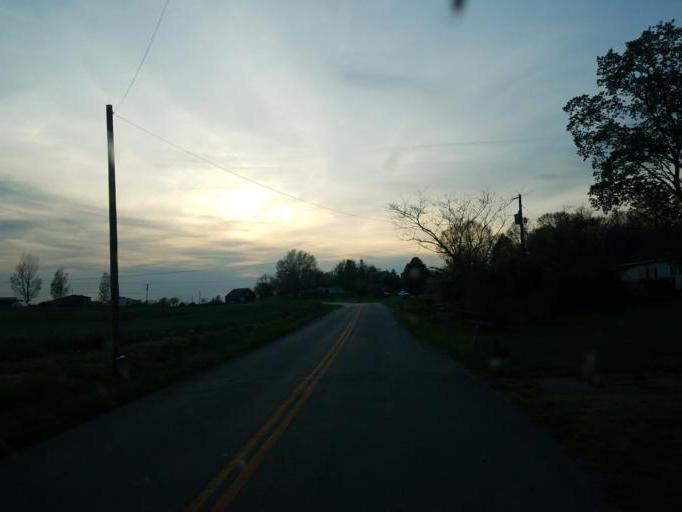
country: US
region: Kentucky
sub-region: Hart County
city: Munfordville
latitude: 37.2332
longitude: -85.7010
